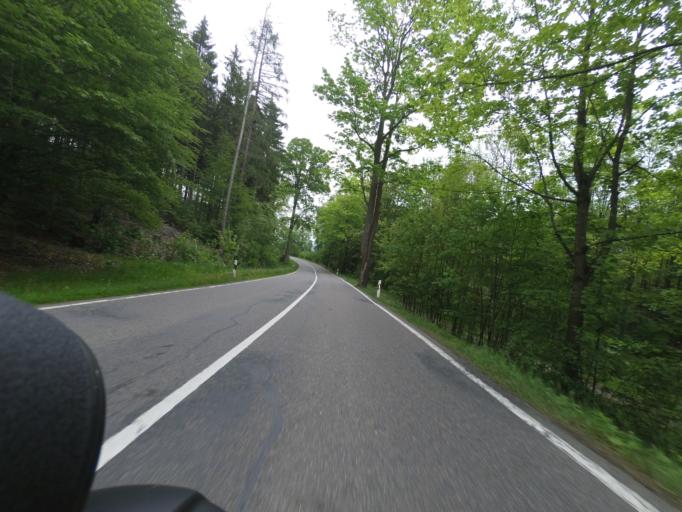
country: DE
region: Saxony
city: Bornichen
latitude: 50.7392
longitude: 13.1615
